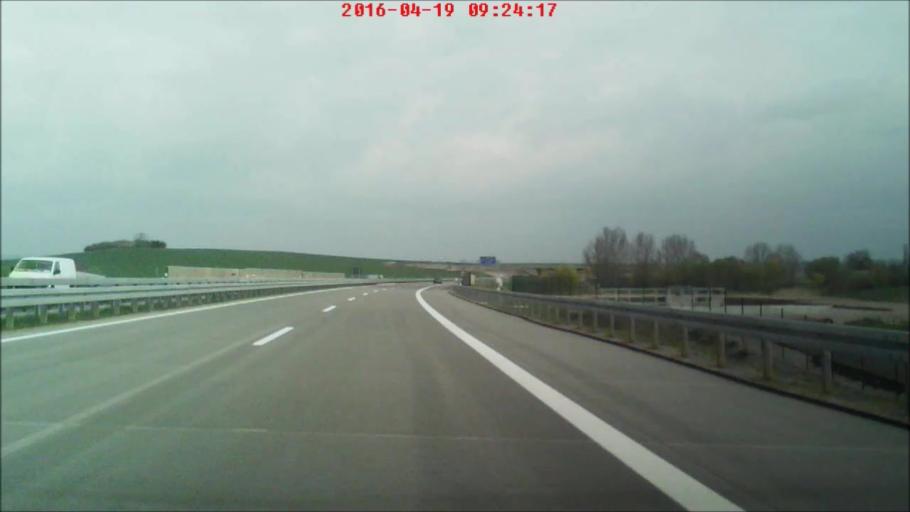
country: DE
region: Thuringia
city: Soemmerda
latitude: 51.1775
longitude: 11.1557
